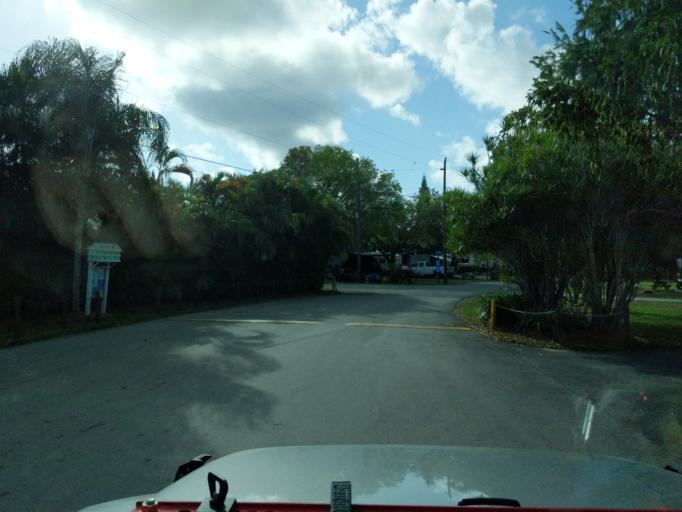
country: US
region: Florida
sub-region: Miami-Dade County
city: Richmond West
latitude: 25.5750
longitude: -80.4519
